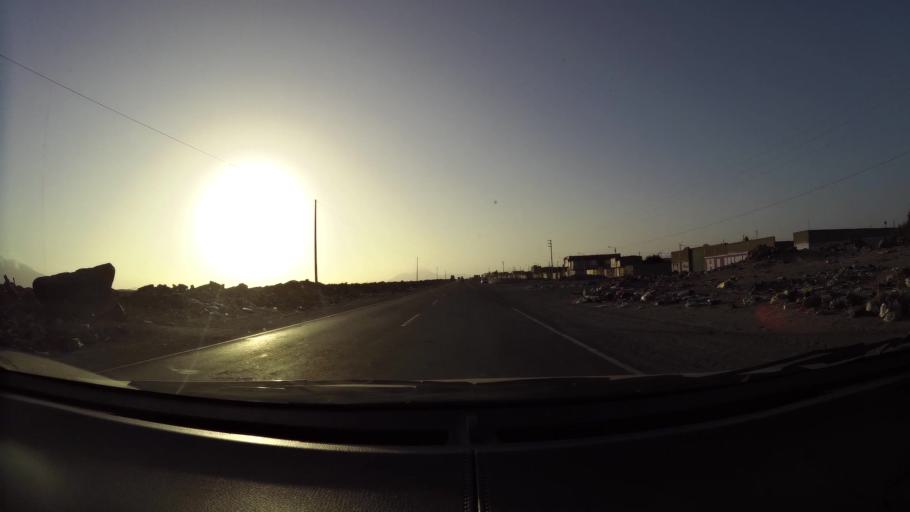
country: PE
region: Ancash
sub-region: Provincia de Santa
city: Buenos Aires
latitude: -9.1522
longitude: -78.5054
